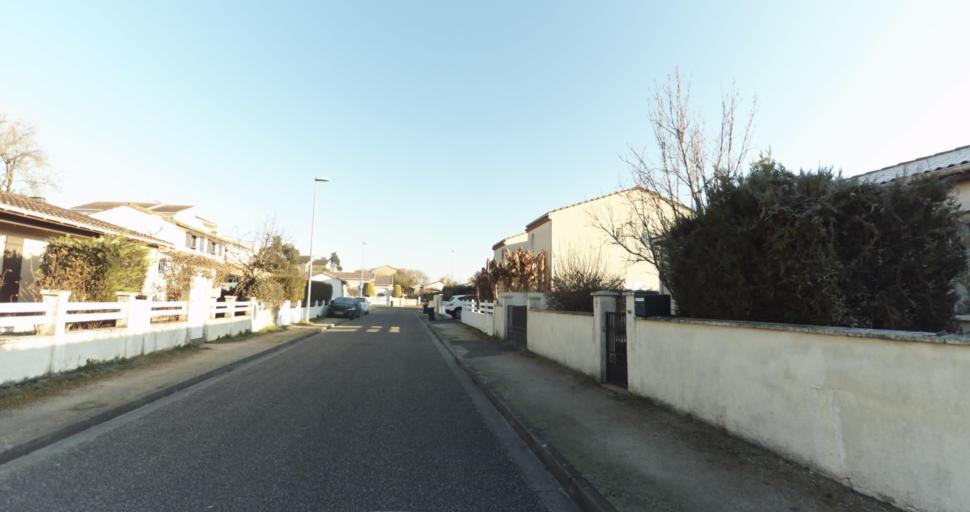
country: FR
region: Aquitaine
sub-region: Departement de la Gironde
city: Carbon-Blanc
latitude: 44.9009
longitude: -0.5056
